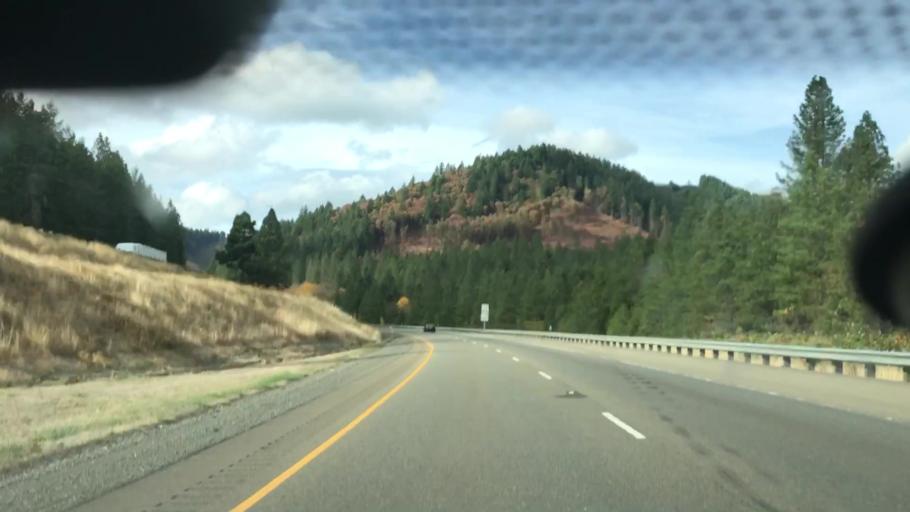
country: US
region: Oregon
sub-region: Douglas County
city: Canyonville
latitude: 42.8060
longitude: -123.2526
